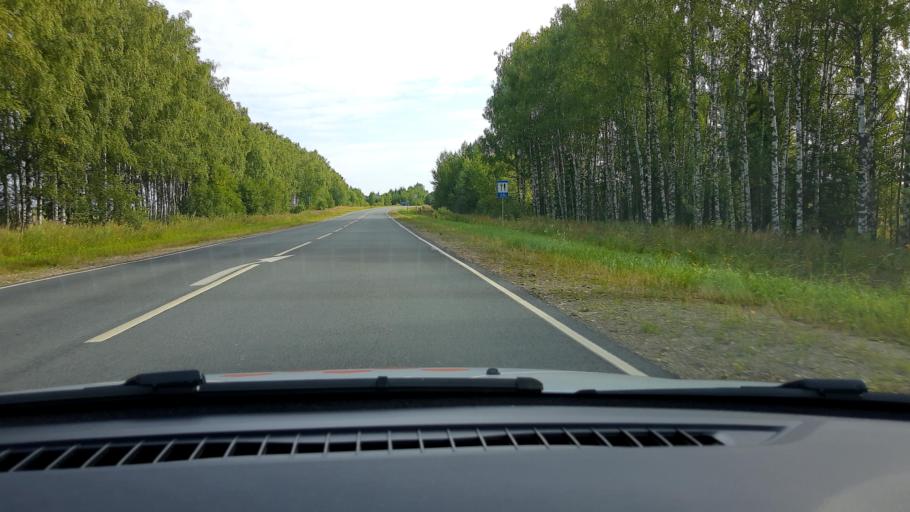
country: RU
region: Nizjnij Novgorod
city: Vladimirskoye
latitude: 56.9544
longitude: 45.0927
